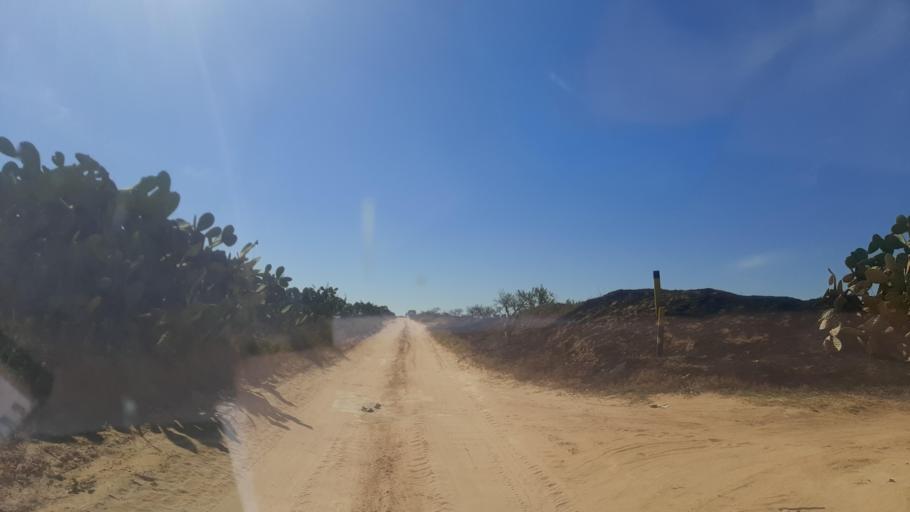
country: TN
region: Safaqis
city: Sfax
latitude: 34.8380
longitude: 10.5587
